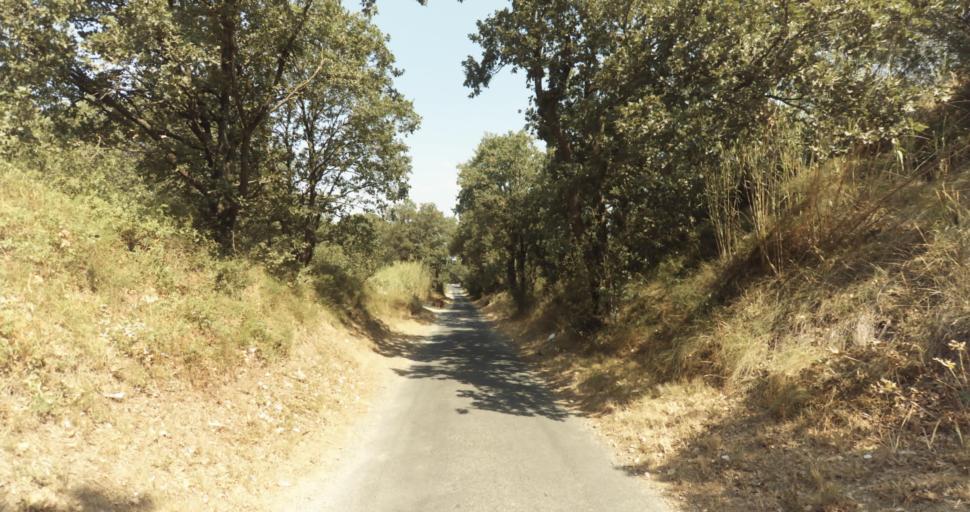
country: FR
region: Languedoc-Roussillon
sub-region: Departement des Pyrenees-Orientales
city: Latour-Bas-Elne
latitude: 42.6122
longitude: 2.9902
